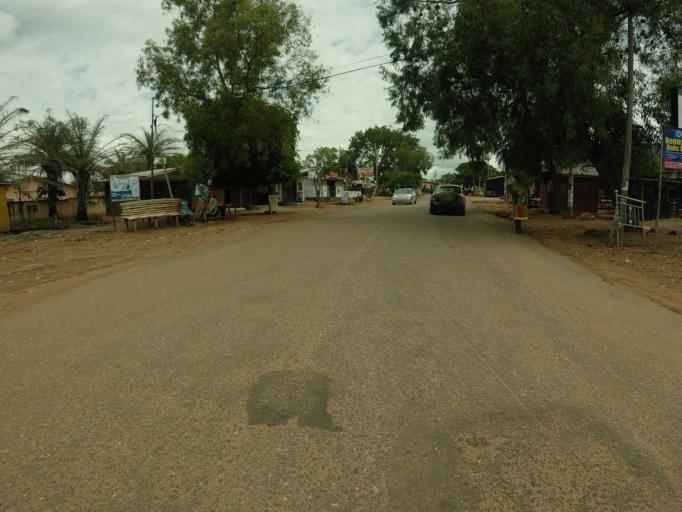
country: GH
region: Volta
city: Ho
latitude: 6.5842
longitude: 0.4629
